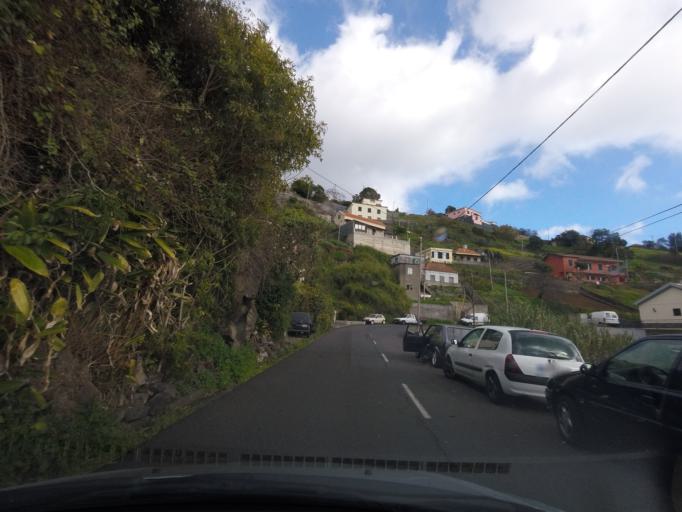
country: PT
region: Madeira
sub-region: Ribeira Brava
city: Campanario
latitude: 32.6631
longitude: -17.0192
